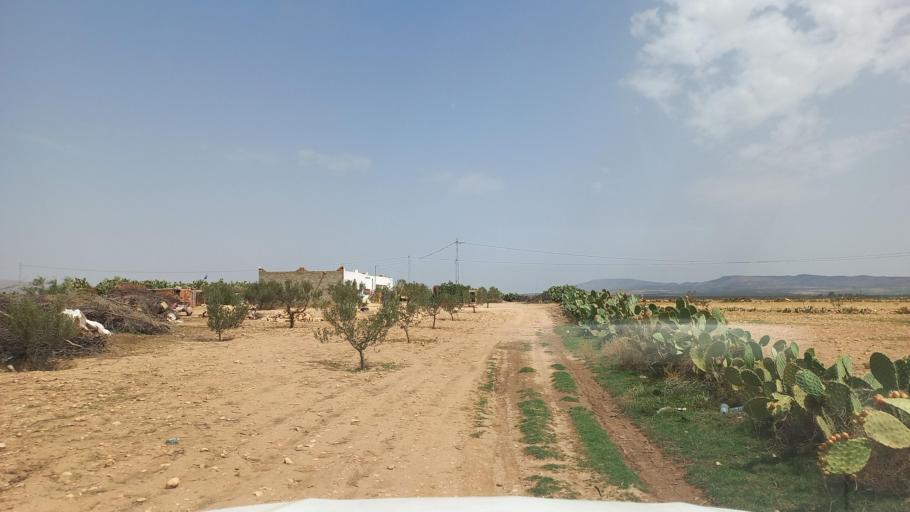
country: TN
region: Al Qasrayn
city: Kasserine
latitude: 35.2890
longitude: 9.0059
